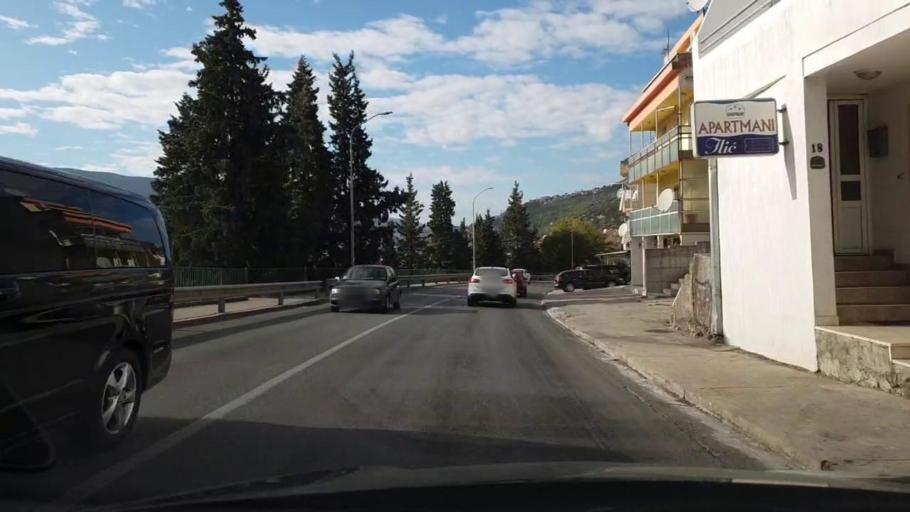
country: ME
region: Herceg Novi
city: Herceg-Novi
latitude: 42.4556
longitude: 18.5282
